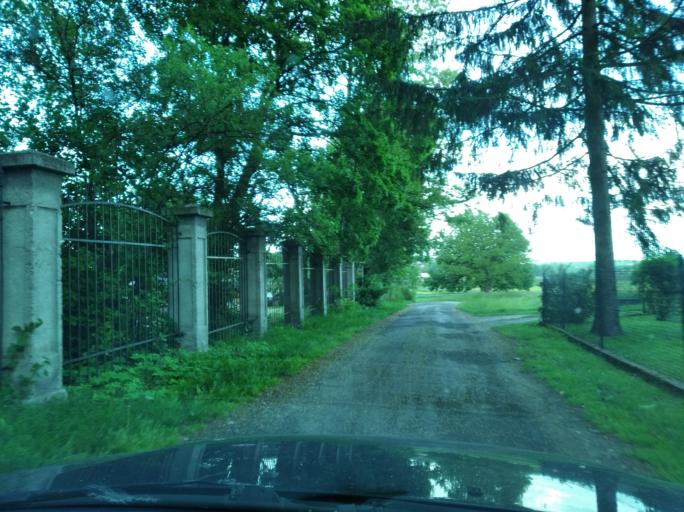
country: PL
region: Subcarpathian Voivodeship
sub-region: Powiat jaroslawski
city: Rokietnica
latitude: 49.9394
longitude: 22.6673
